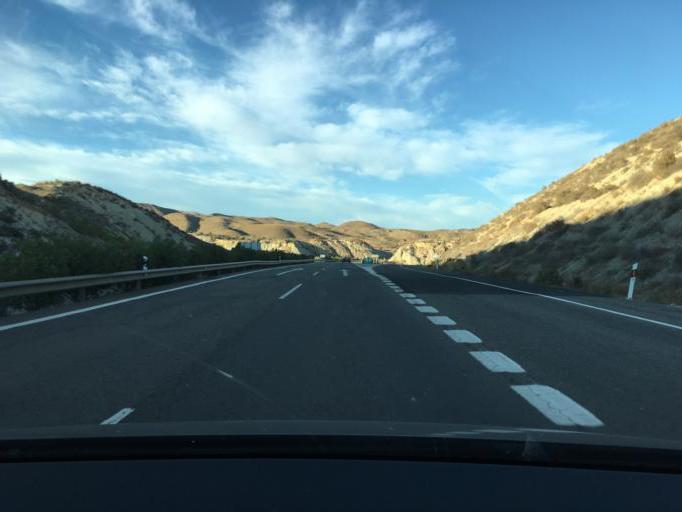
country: ES
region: Andalusia
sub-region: Provincia de Almeria
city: Bedar
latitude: 37.1273
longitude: -2.0132
